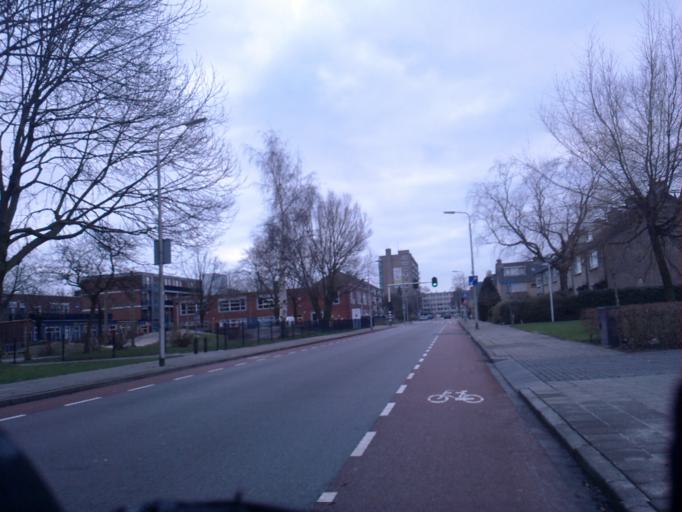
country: NL
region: Utrecht
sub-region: Gemeente Amersfoort
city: Randenbroek
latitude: 52.1559
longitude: 5.4136
